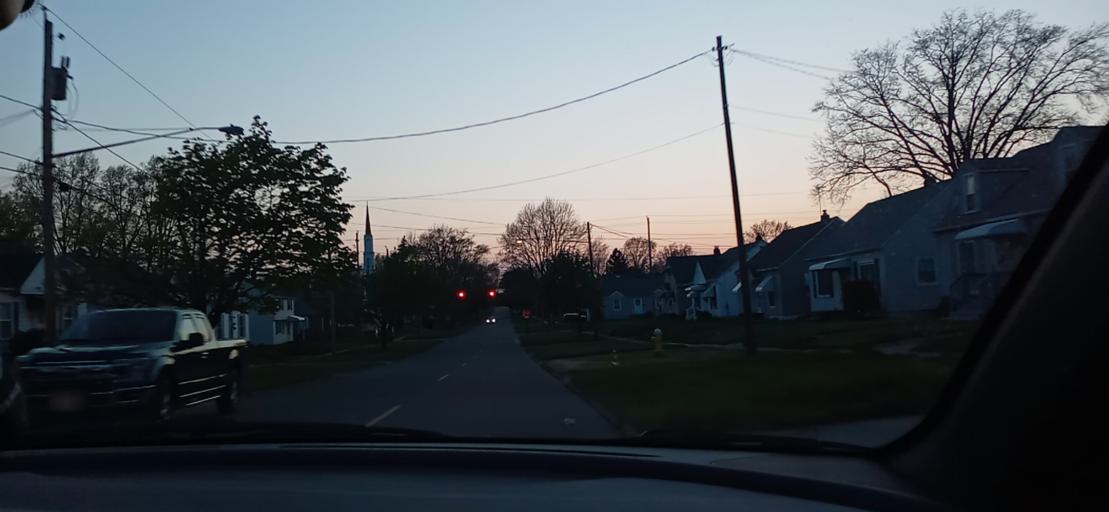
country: US
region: Ohio
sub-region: Summit County
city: Akron
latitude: 41.0445
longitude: -81.4988
